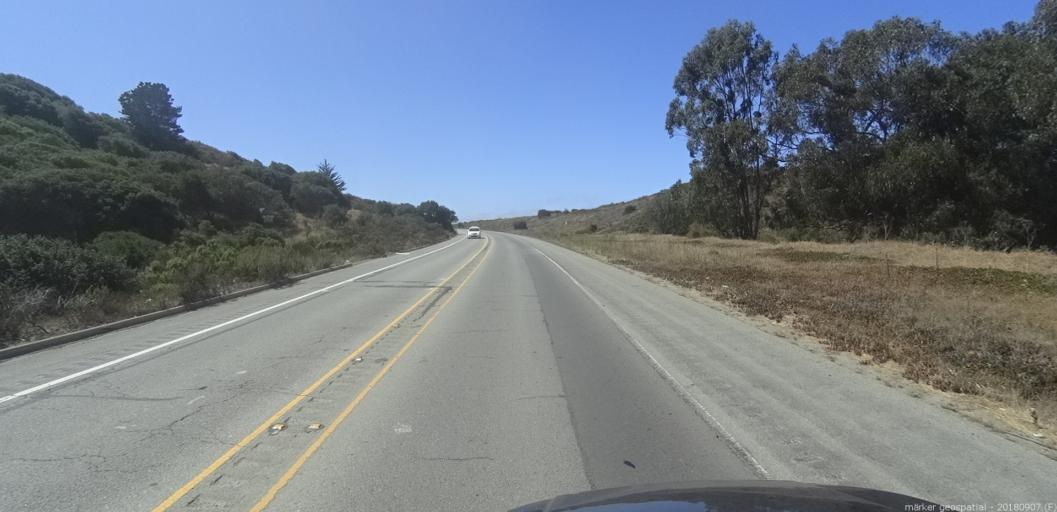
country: US
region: California
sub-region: Monterey County
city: Marina
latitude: 36.6763
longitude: -121.7492
